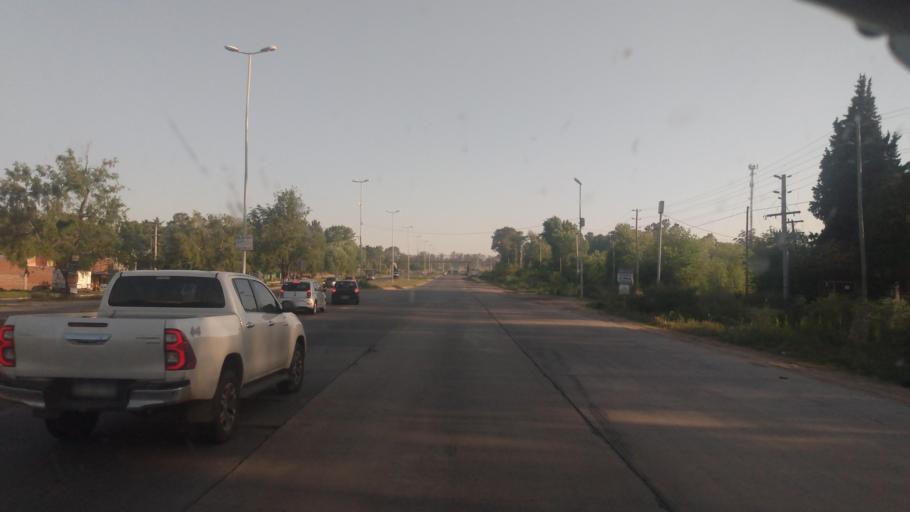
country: AR
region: Buenos Aires
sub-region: Partido de Campana
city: Campana
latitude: -34.2478
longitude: -58.9658
